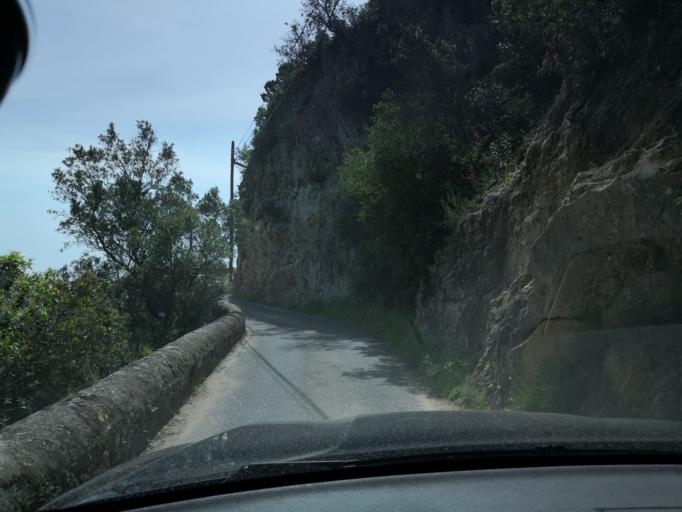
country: PT
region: Setubal
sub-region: Palmela
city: Quinta do Anjo
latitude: 38.4741
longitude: -8.9833
